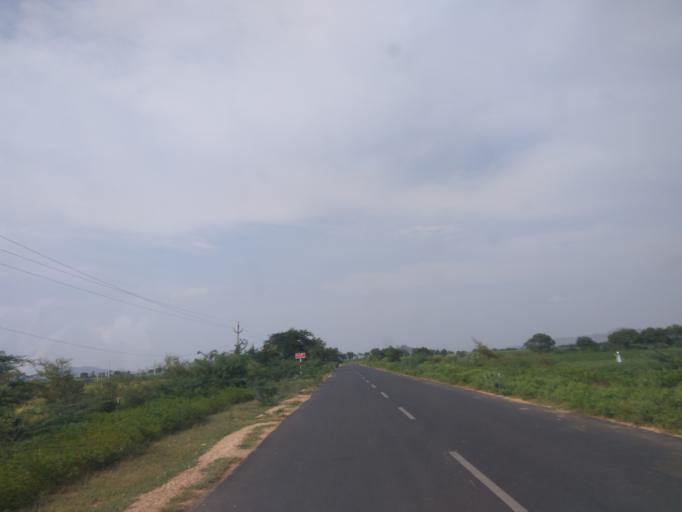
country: IN
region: Andhra Pradesh
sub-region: Prakasam
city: Markapur
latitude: 15.7723
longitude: 79.2417
